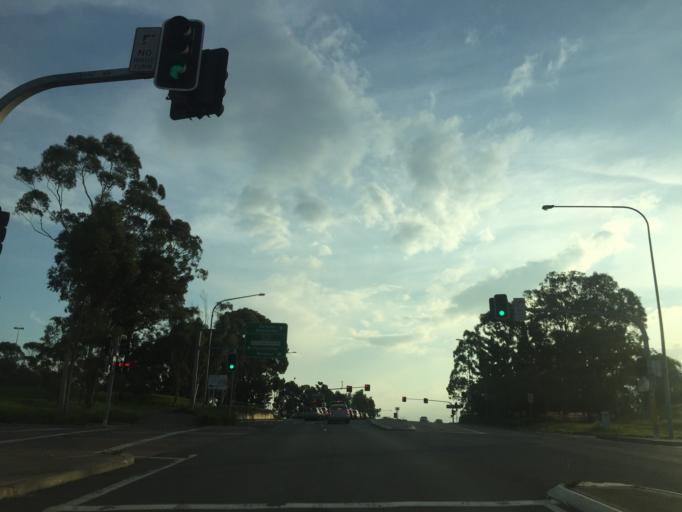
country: AU
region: New South Wales
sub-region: Blacktown
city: Stanhope Gardens
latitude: -33.7200
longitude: 150.9393
